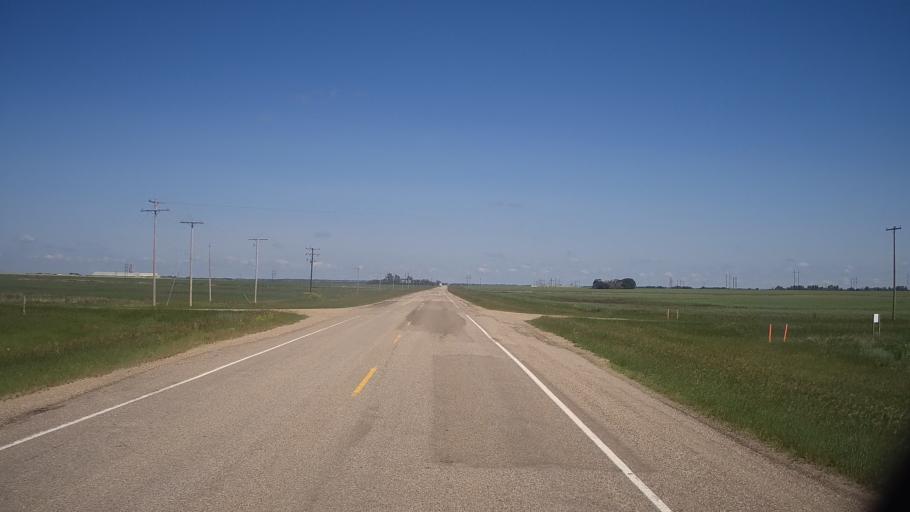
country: CA
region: Saskatchewan
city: Saskatoon
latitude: 51.9685
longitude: -106.0752
